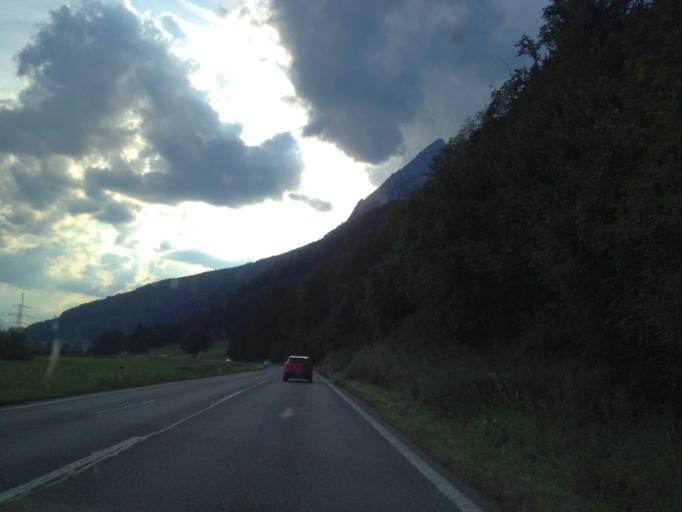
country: AT
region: Styria
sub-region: Politischer Bezirk Liezen
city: Irdning
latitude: 47.5128
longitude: 14.0669
